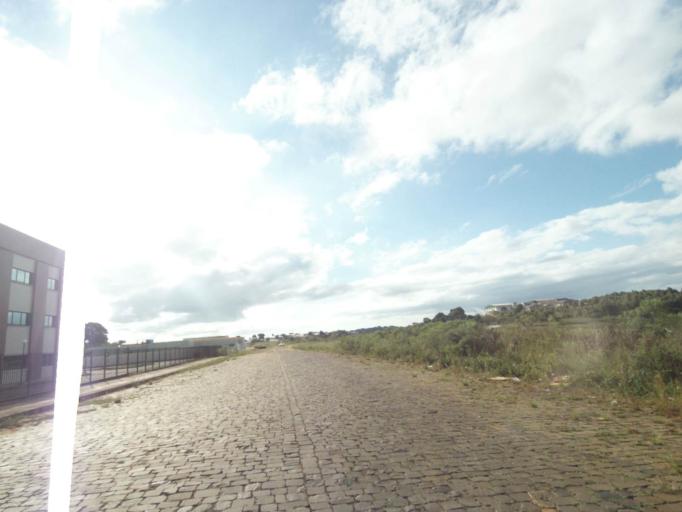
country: BR
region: Rio Grande do Sul
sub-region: Lagoa Vermelha
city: Lagoa Vermelha
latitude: -28.2017
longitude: -51.5201
